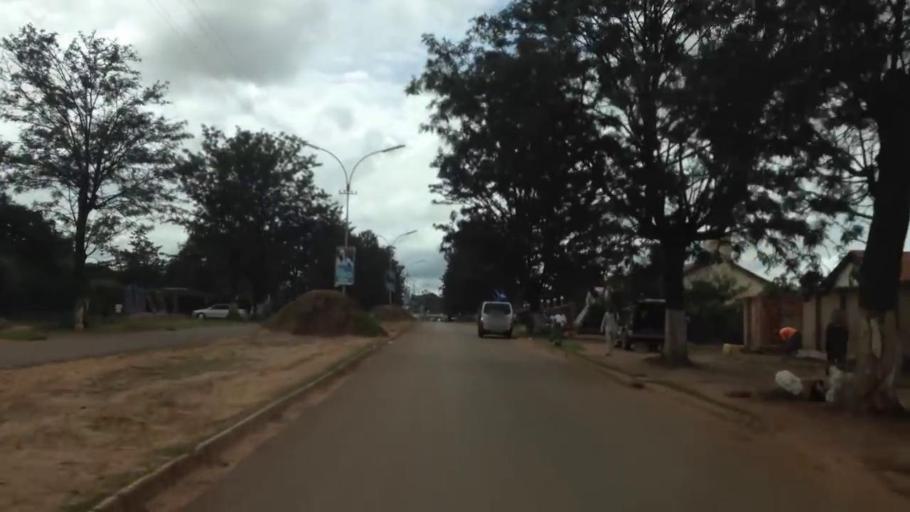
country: CD
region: Katanga
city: Kolwezi
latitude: -10.7191
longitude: 25.5011
